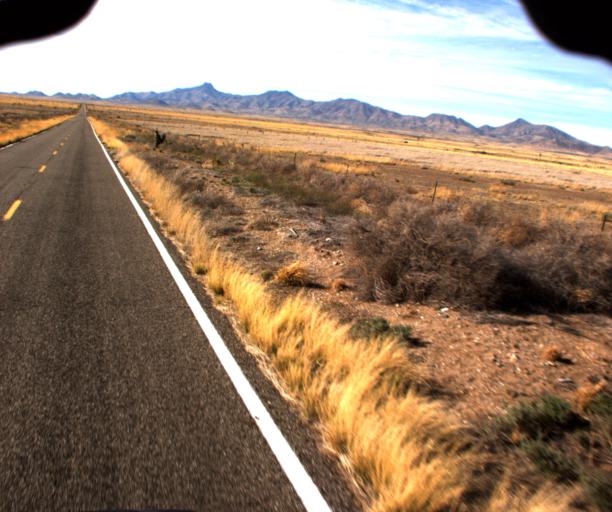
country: US
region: Arizona
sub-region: Cochise County
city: Willcox
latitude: 32.0670
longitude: -109.5079
